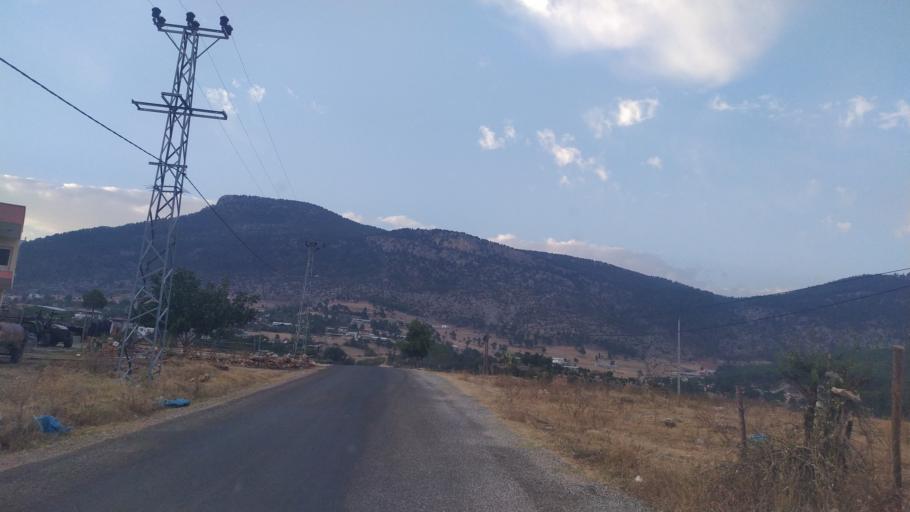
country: TR
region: Mersin
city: Camliyayla
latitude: 37.2349
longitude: 34.7181
